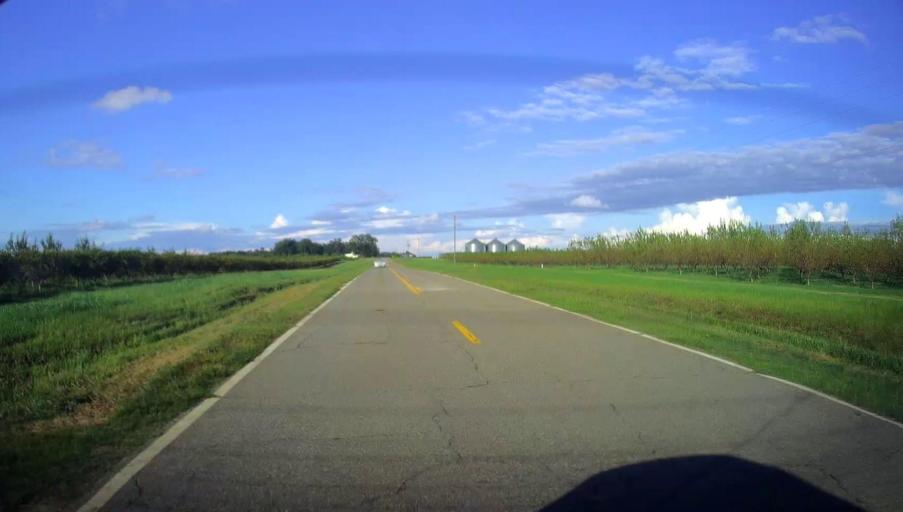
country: US
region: Georgia
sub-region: Bleckley County
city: Cochran
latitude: 32.3954
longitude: -83.4412
